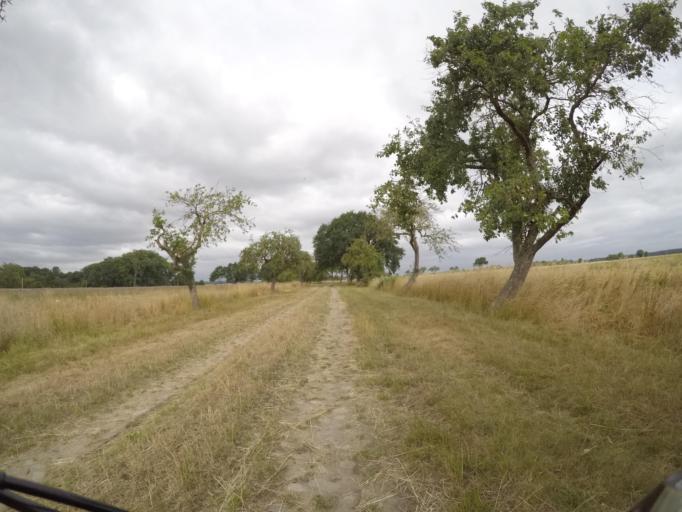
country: DE
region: Lower Saxony
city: Hitzacker
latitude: 53.1710
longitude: 11.0410
